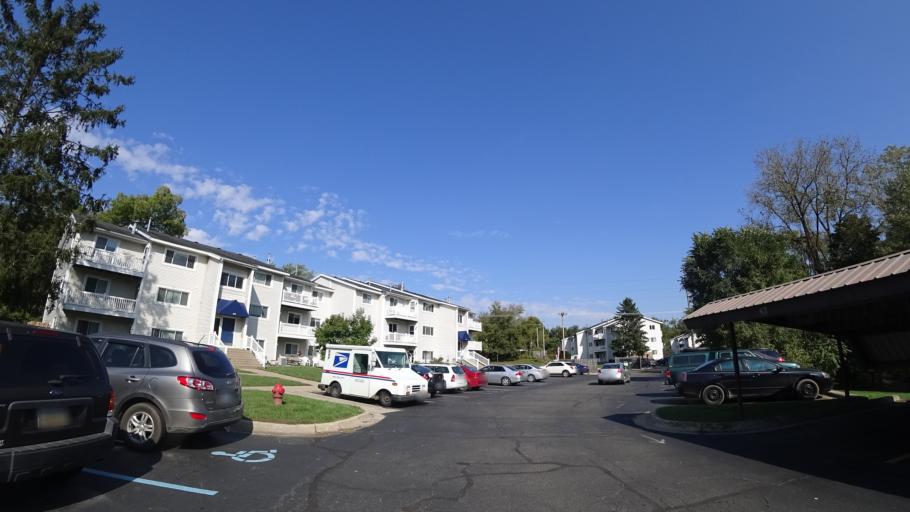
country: US
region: Michigan
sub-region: Saint Joseph County
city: Three Rivers
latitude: 41.9375
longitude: -85.6352
